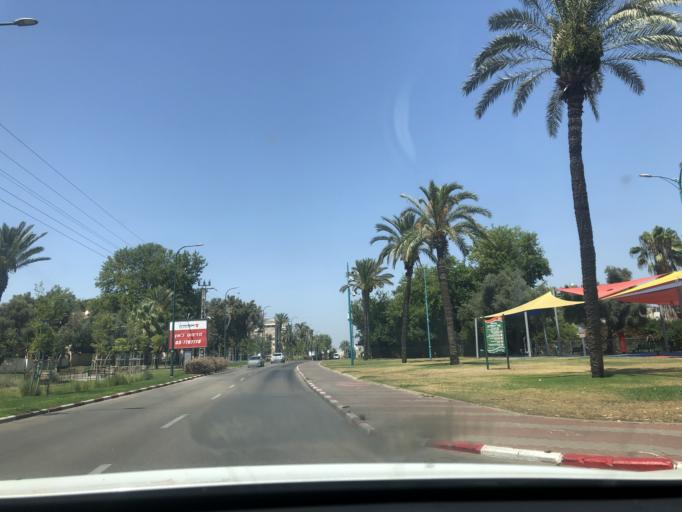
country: IL
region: Central District
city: Lod
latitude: 31.9412
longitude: 34.8878
